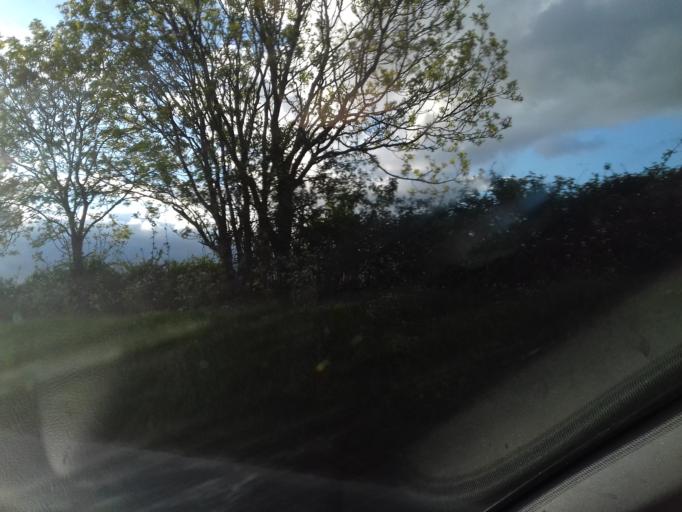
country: IE
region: Leinster
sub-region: South Dublin
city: Rathcoole
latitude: 53.2943
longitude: -6.4837
